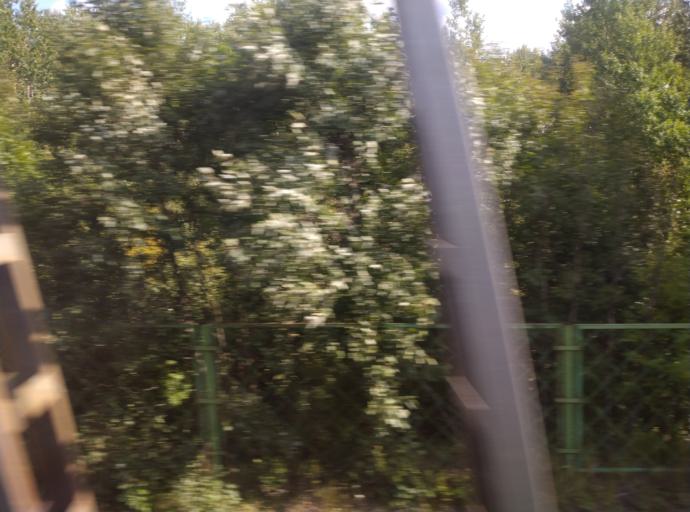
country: RU
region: Leningrad
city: Krasnyy Bor
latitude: 59.6778
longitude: 30.7050
